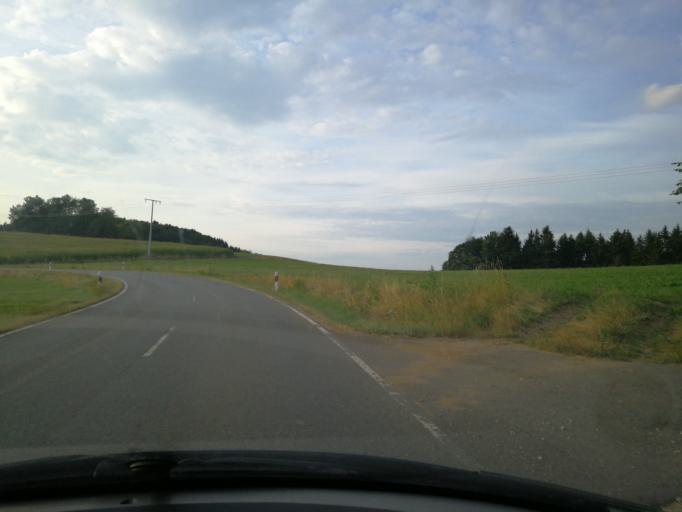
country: DE
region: Bavaria
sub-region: Upper Palatinate
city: Falkenstein
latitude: 49.0876
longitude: 12.5039
